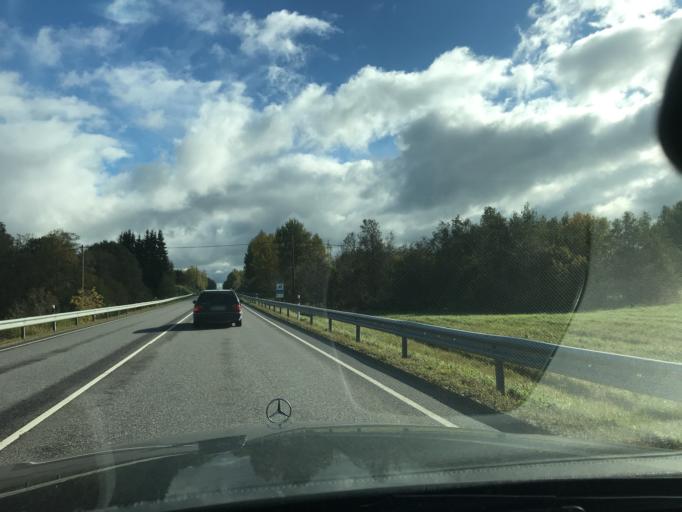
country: EE
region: Vorumaa
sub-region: Voru linn
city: Voru
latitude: 57.7795
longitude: 27.1149
